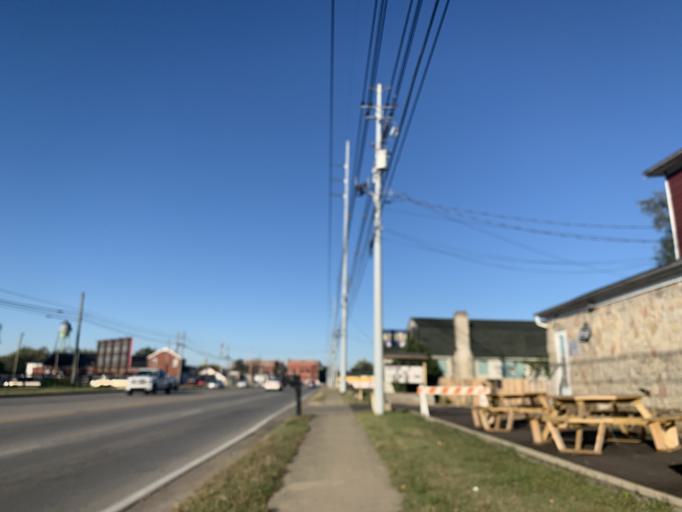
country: US
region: Kentucky
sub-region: Jefferson County
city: Shively
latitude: 38.2079
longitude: -85.7881
